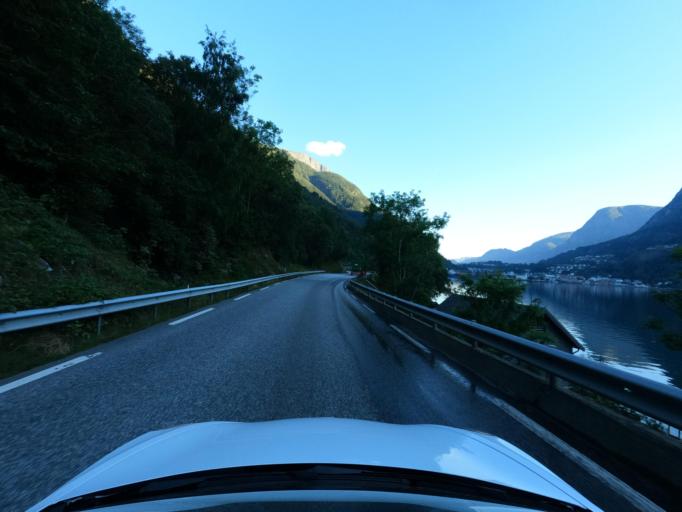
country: NO
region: Hordaland
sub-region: Odda
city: Odda
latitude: 60.0822
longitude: 6.5500
